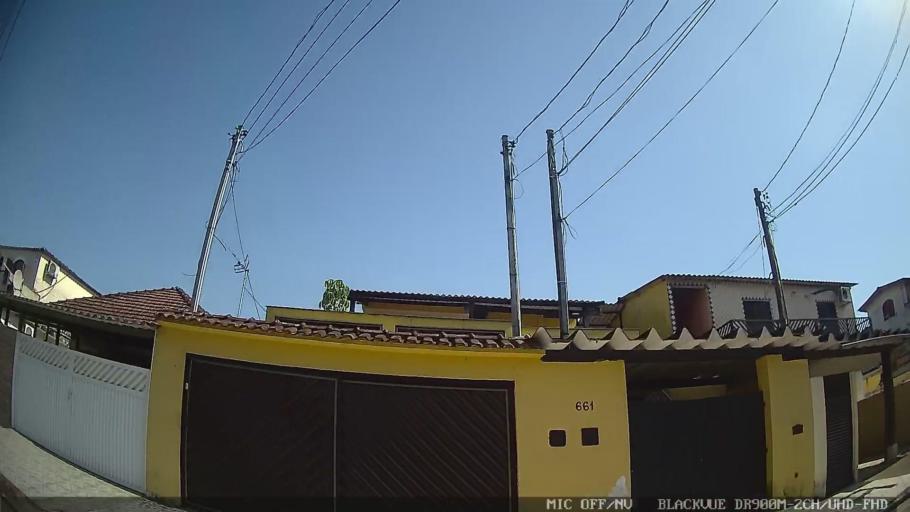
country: BR
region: Sao Paulo
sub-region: Santos
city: Santos
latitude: -23.9346
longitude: -46.3046
